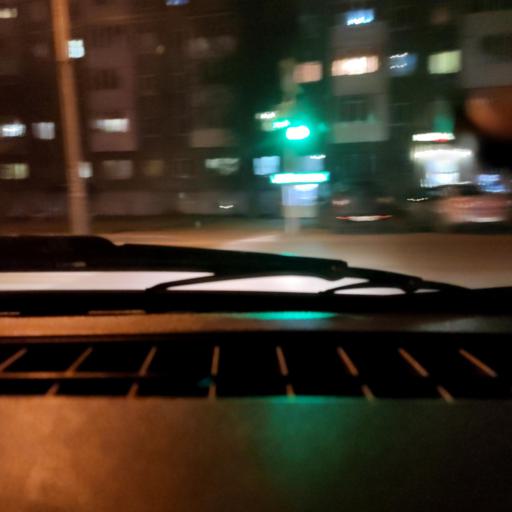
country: RU
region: Bashkortostan
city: Ufa
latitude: 54.8086
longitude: 56.1155
